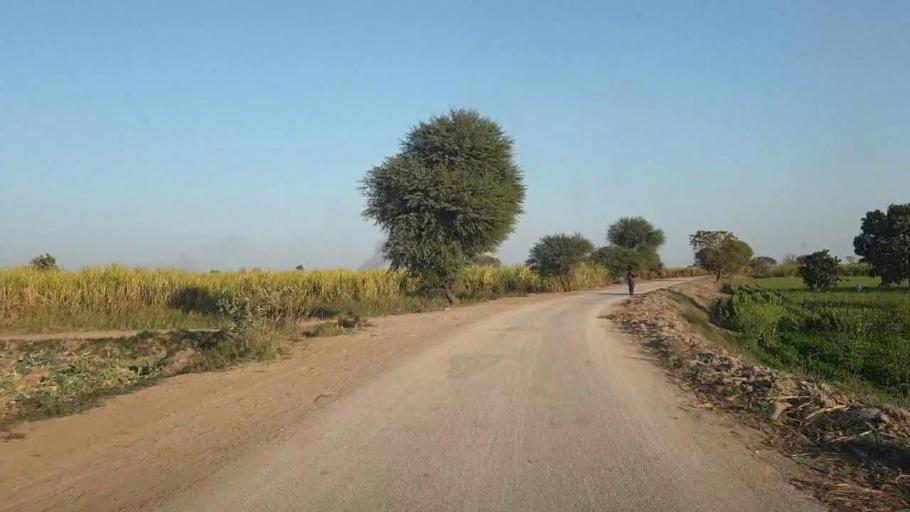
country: PK
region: Sindh
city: Tando Allahyar
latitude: 25.3539
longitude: 68.7214
